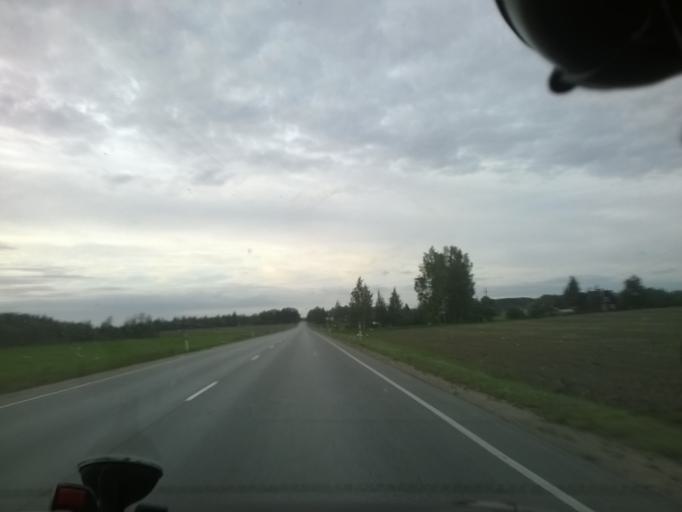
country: EE
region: Vorumaa
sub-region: Voru linn
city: Voru
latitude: 57.9089
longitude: 26.8269
